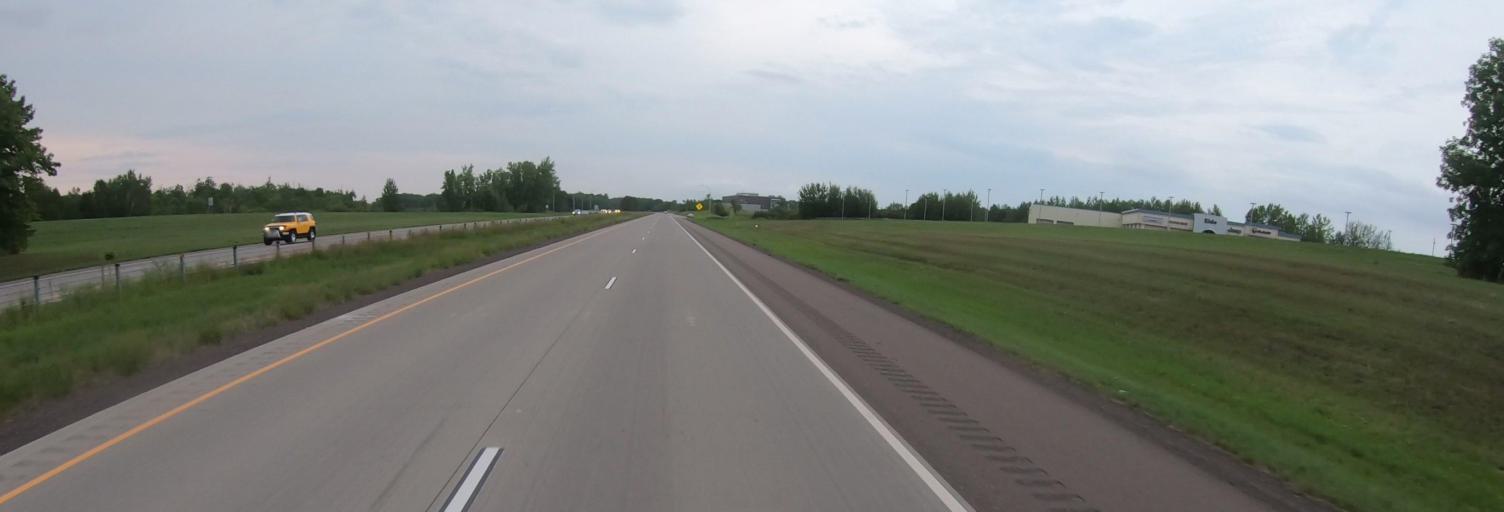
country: US
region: Minnesota
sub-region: Pine County
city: Pine City
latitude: 45.8478
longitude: -92.9751
